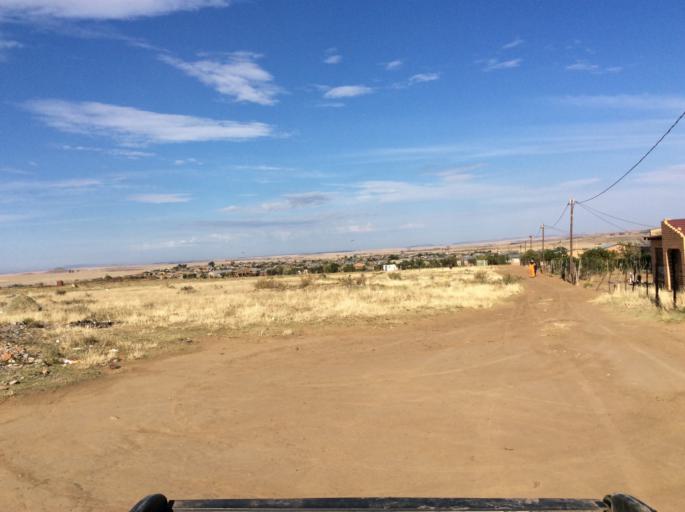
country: LS
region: Mafeteng
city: Mafeteng
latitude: -29.7098
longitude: 27.0168
